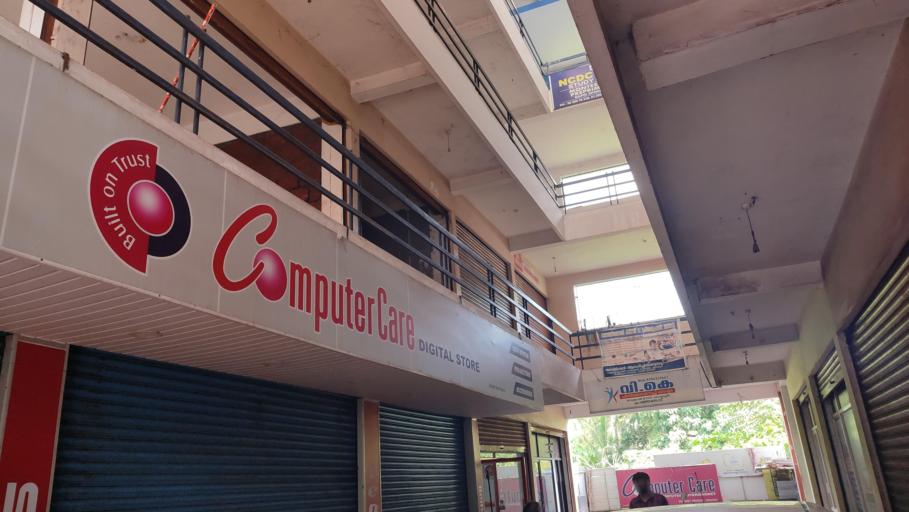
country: IN
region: Kerala
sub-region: Kasaragod District
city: Kannangad
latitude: 12.3246
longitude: 75.0866
